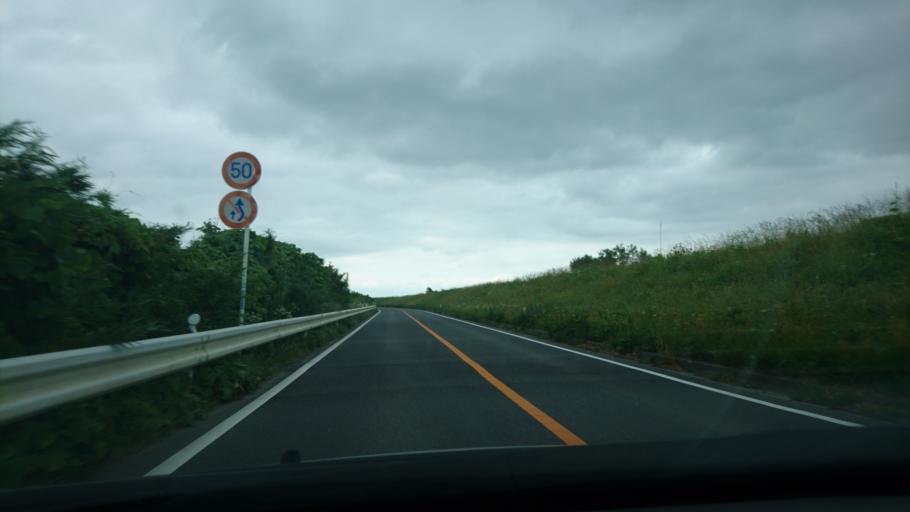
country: JP
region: Iwate
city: Ichinoseki
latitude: 38.7380
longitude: 141.1519
